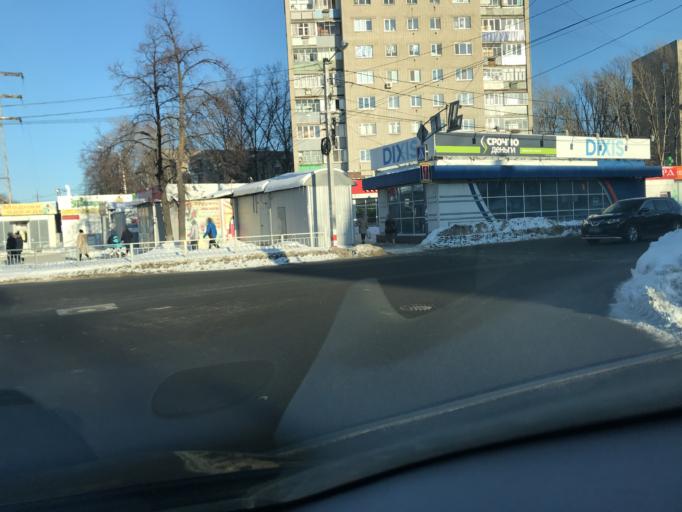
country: RU
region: Ulyanovsk
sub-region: Ulyanovskiy Rayon
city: Ulyanovsk
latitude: 54.3525
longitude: 48.3624
